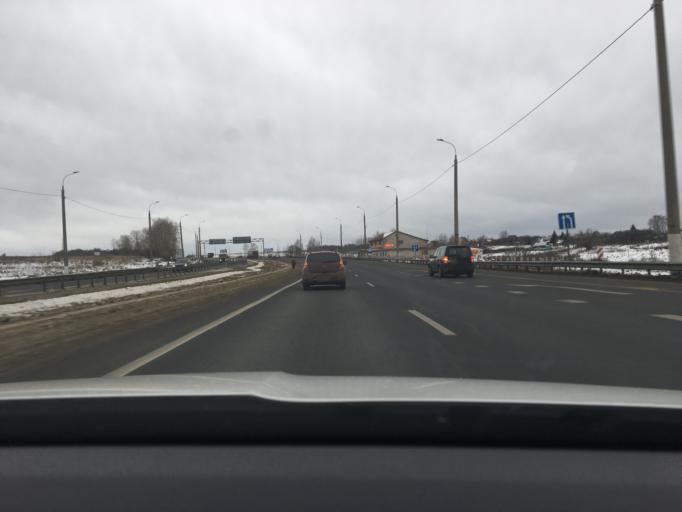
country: RU
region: Moskovskaya
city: Serpukhov
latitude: 54.8543
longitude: 37.4737
